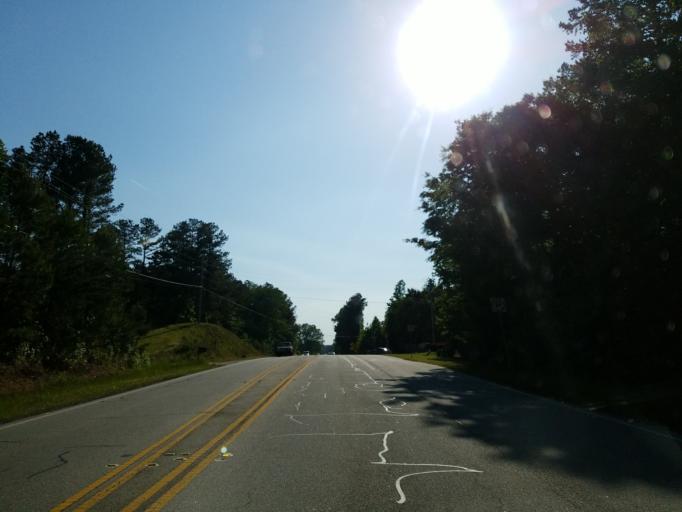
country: US
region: Georgia
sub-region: Carroll County
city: Villa Rica
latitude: 33.8525
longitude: -84.9425
